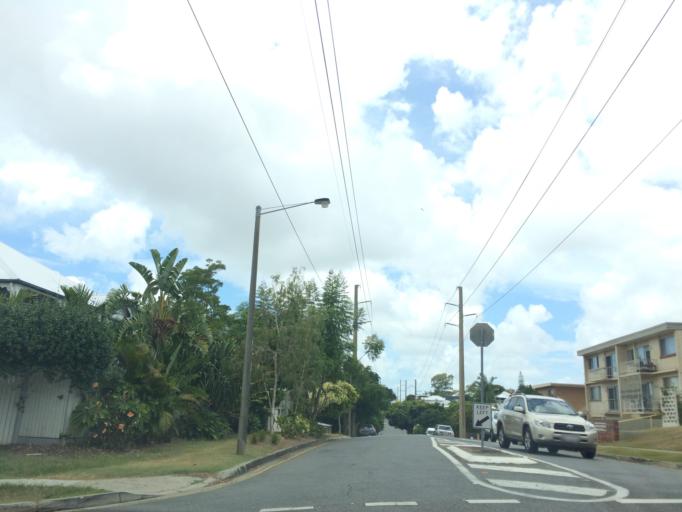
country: AU
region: Queensland
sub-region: Brisbane
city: Balmoral
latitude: -27.4478
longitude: 153.0562
